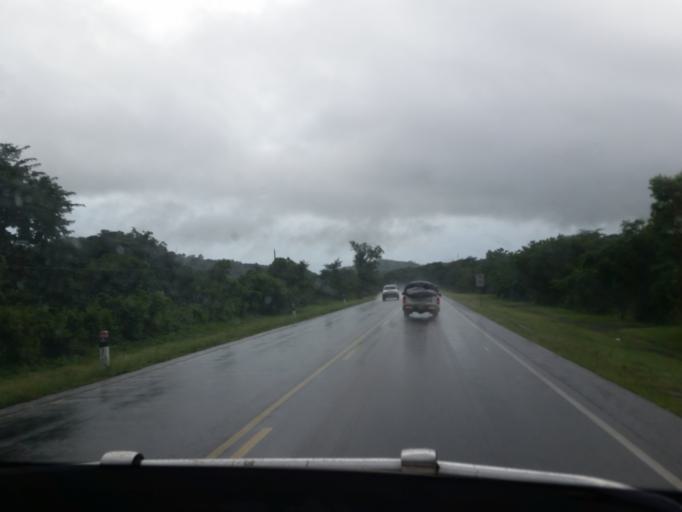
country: NI
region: Matagalpa
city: Ciudad Dario
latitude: 12.5989
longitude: -86.0454
